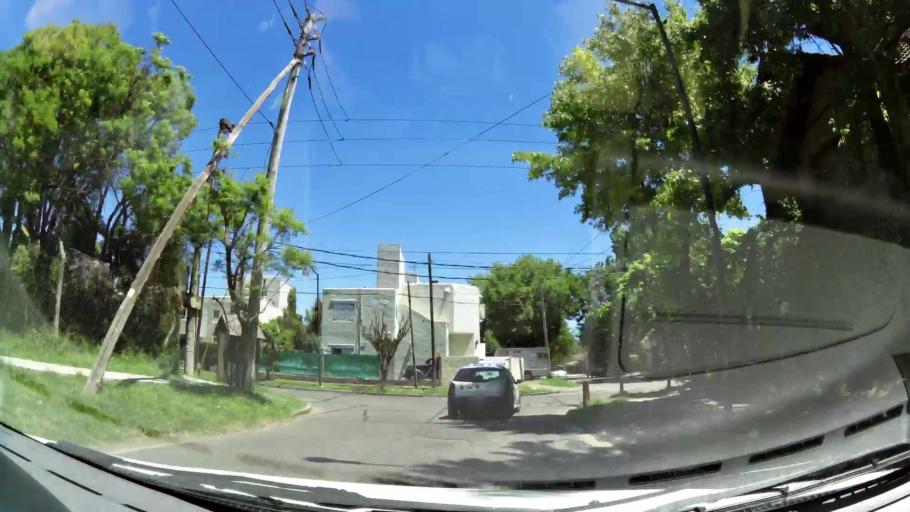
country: AR
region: Buenos Aires
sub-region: Partido de San Isidro
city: San Isidro
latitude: -34.4965
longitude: -58.5724
